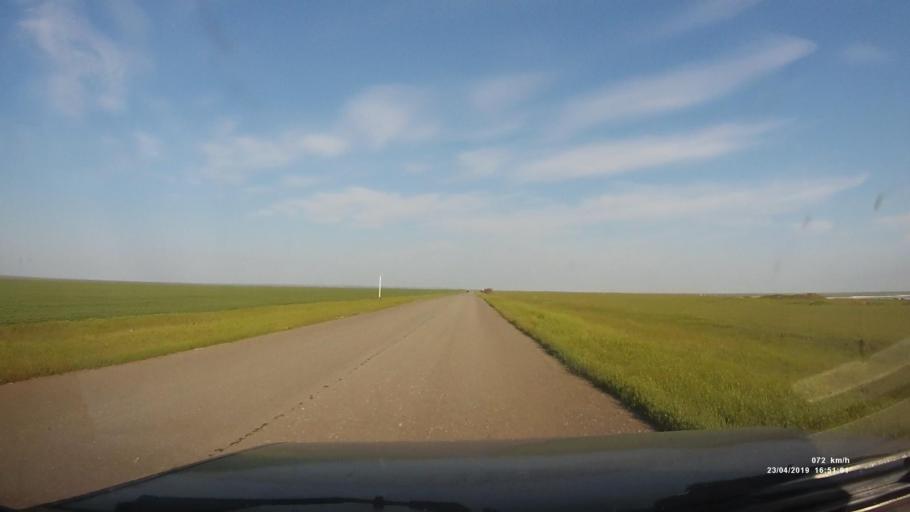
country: RU
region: Kalmykiya
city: Priyutnoye
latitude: 46.3247
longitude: 43.3000
